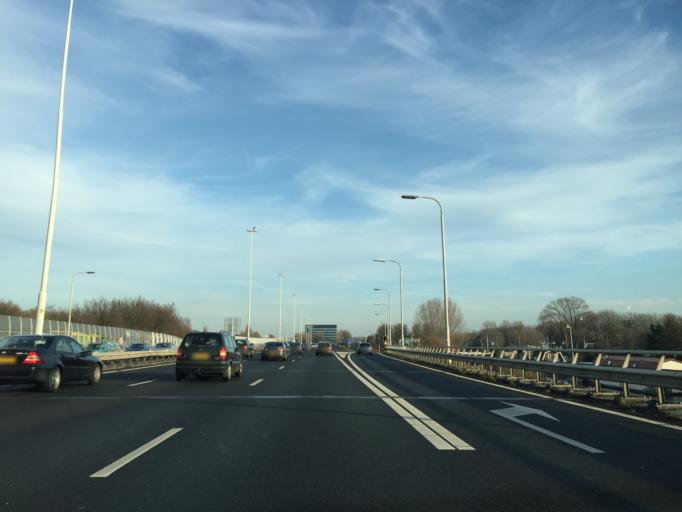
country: NL
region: South Holland
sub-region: Gemeente Rotterdam
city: Rotterdam
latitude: 51.9416
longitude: 4.4808
